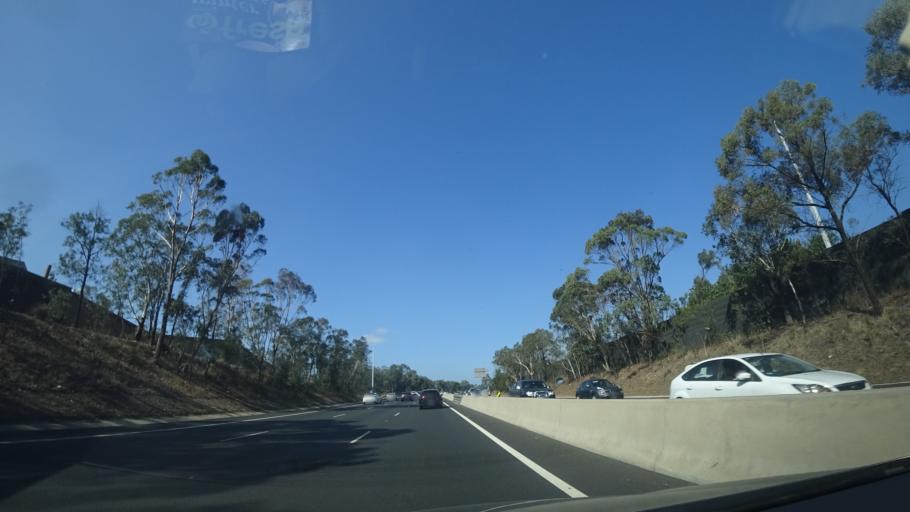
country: AU
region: New South Wales
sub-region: Bankstown
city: Revesby
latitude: -33.9415
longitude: 151.0029
